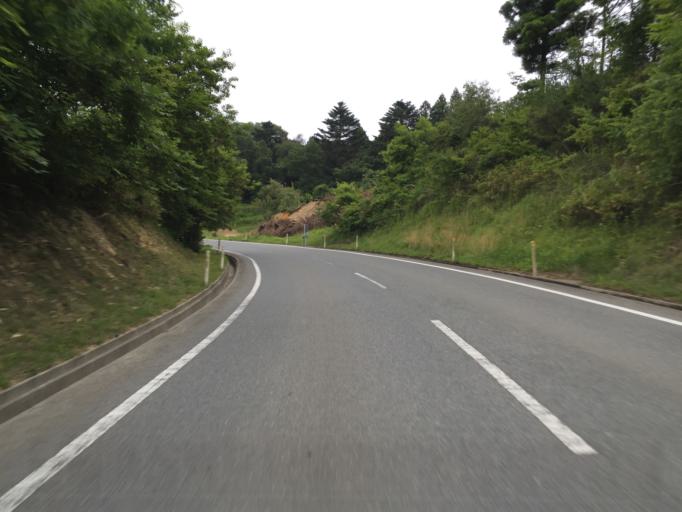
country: JP
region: Fukushima
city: Namie
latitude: 37.6747
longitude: 141.0082
